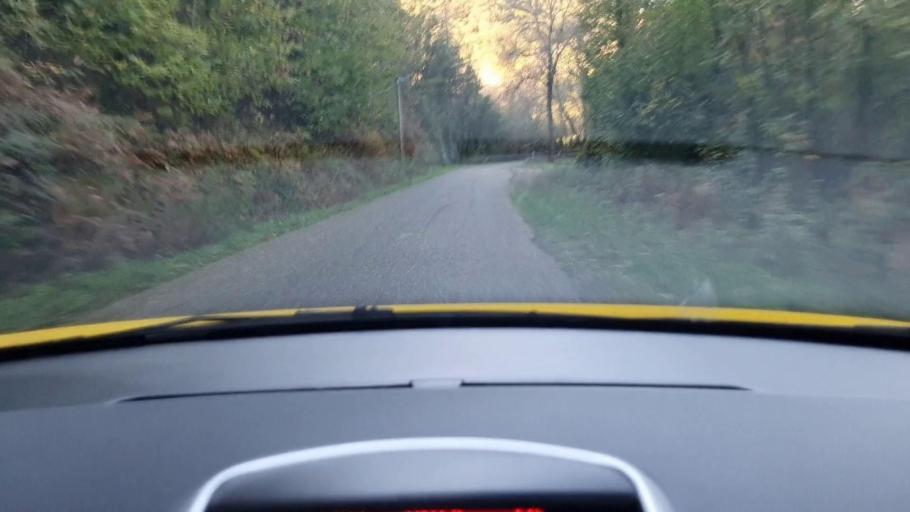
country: FR
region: Languedoc-Roussillon
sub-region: Departement du Gard
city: Sumene
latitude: 43.9891
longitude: 3.6823
